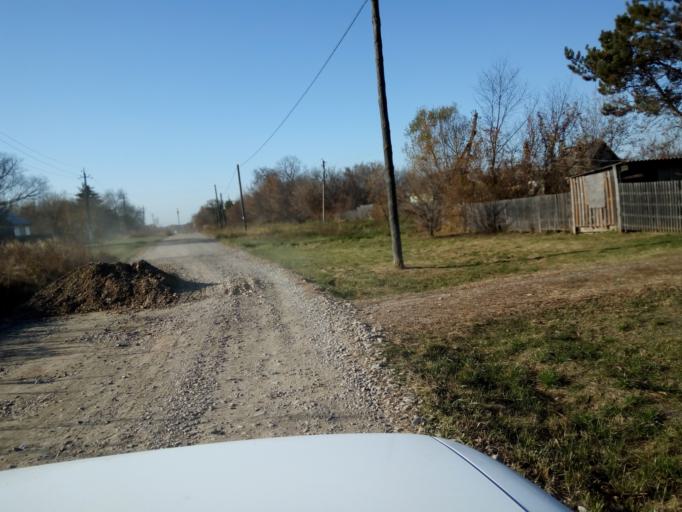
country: RU
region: Primorskiy
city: Lazo
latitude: 45.8714
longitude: 133.6513
